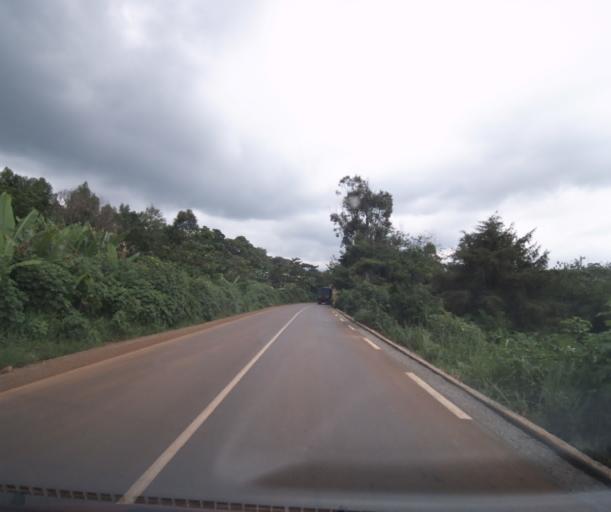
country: CM
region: West
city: Mbouda
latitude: 5.6627
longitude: 10.2240
